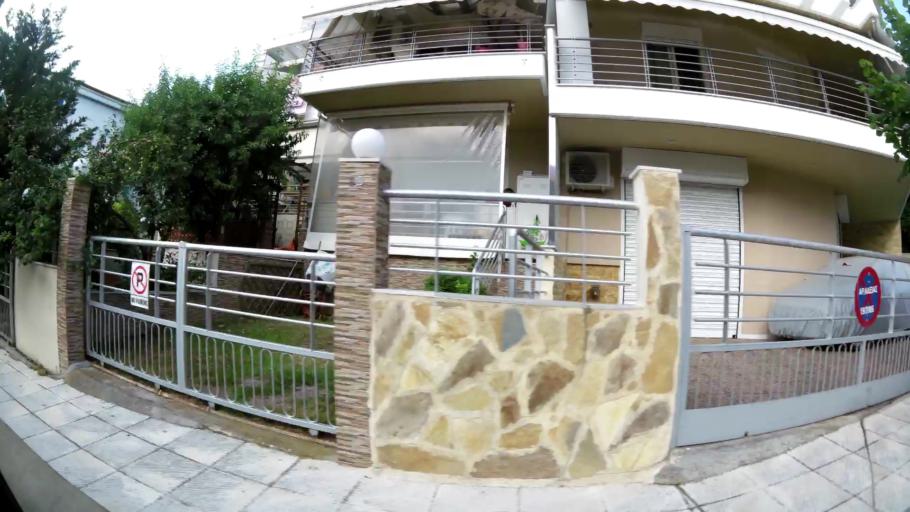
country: GR
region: Central Macedonia
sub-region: Nomos Thessalonikis
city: Pefka
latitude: 40.6556
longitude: 23.0020
